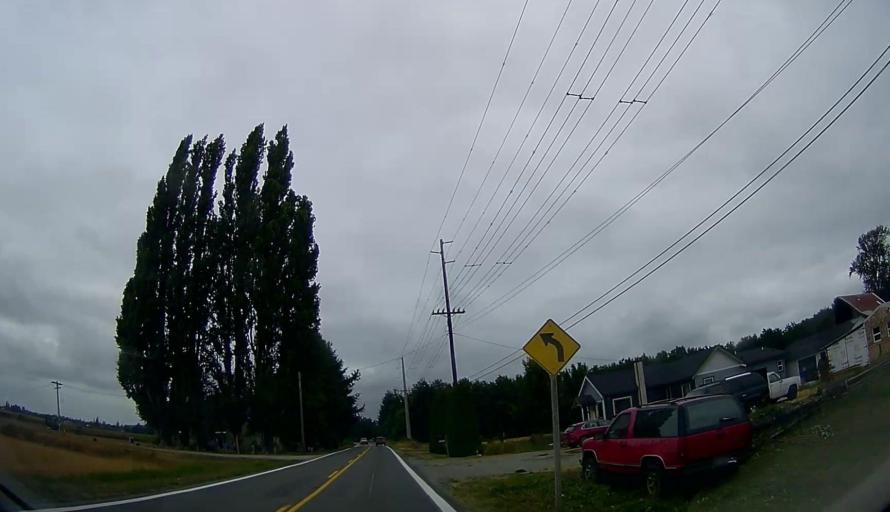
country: US
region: Washington
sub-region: Snohomish County
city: Stanwood
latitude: 48.2165
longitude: -122.3349
